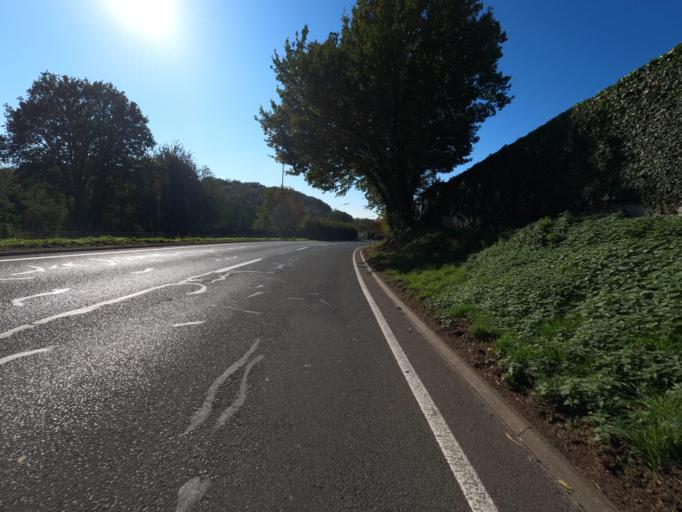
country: DE
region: North Rhine-Westphalia
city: Huckelhoven
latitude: 51.0508
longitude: 6.2534
